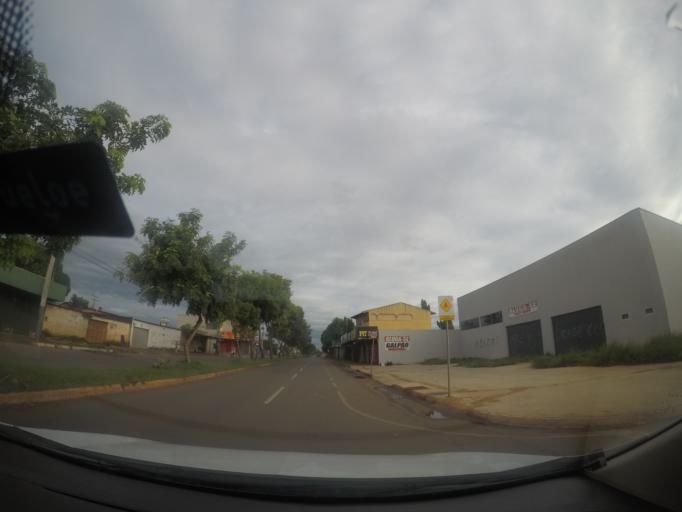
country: BR
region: Goias
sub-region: Goiania
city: Goiania
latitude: -16.6225
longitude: -49.3371
